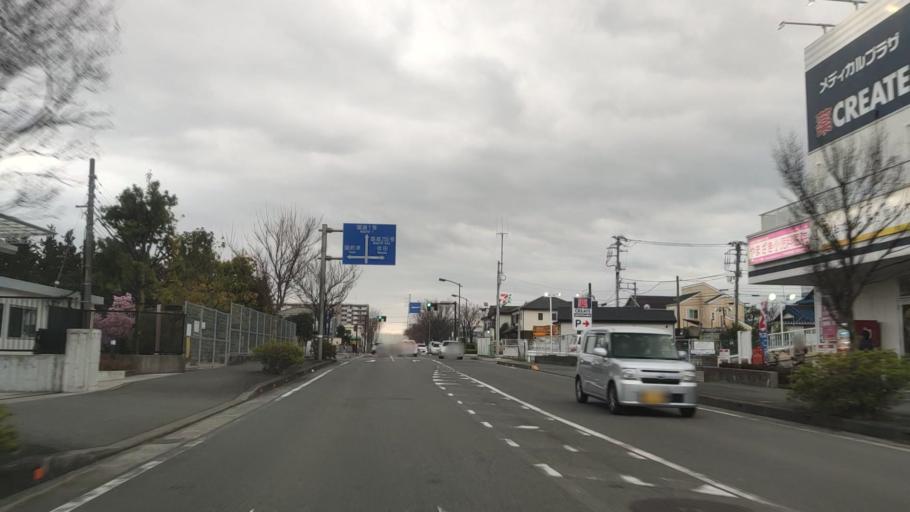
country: JP
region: Kanagawa
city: Odawara
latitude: 35.2863
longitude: 139.1893
